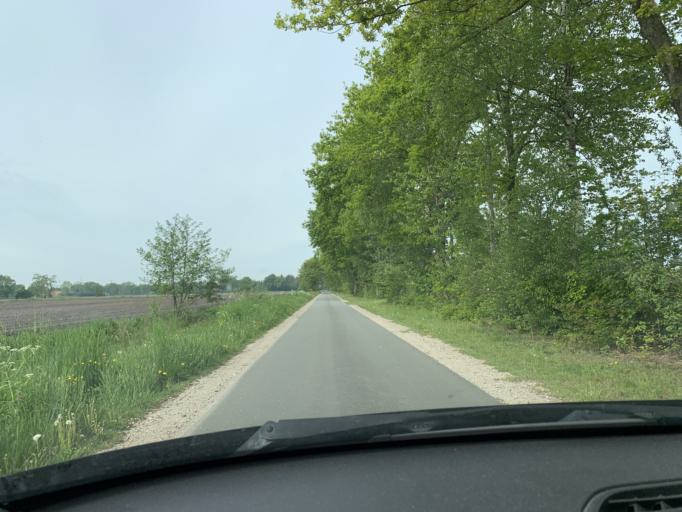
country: DE
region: Lower Saxony
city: Apen
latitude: 53.2103
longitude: 7.7724
